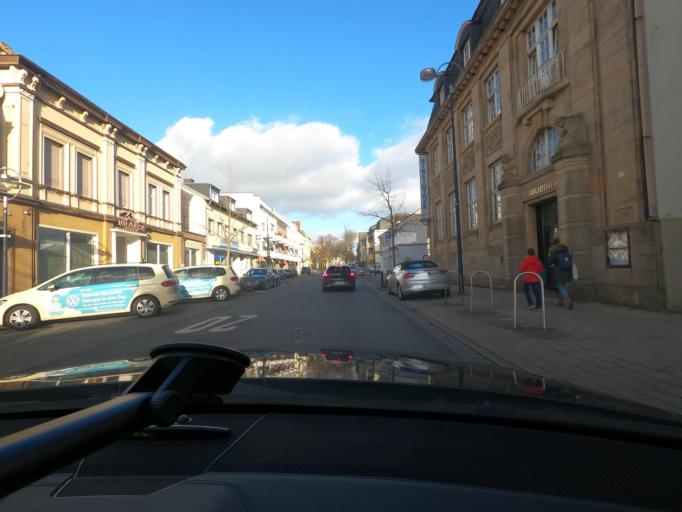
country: DE
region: North Rhine-Westphalia
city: Schwerte
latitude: 51.4935
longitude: 7.5579
